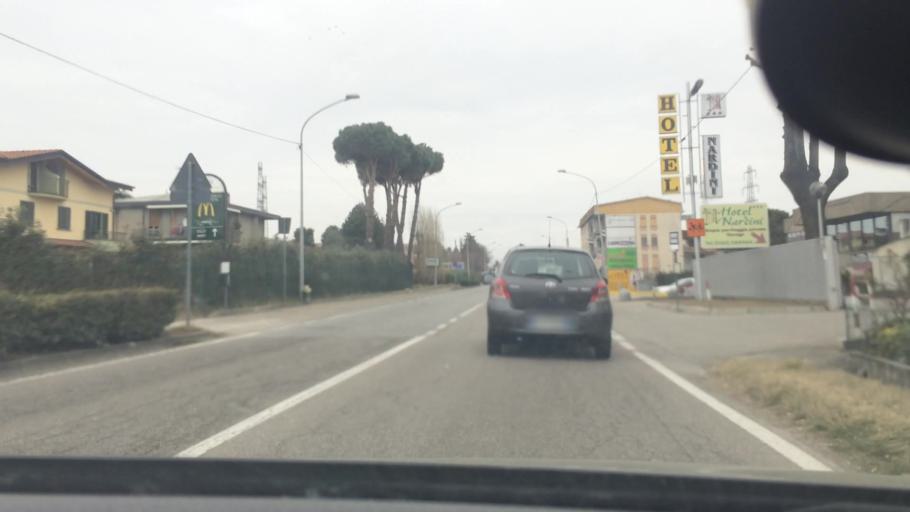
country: IT
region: Lombardy
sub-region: Provincia di Monza e Brianza
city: Lentate sul Seveso
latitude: 45.6835
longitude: 9.1114
